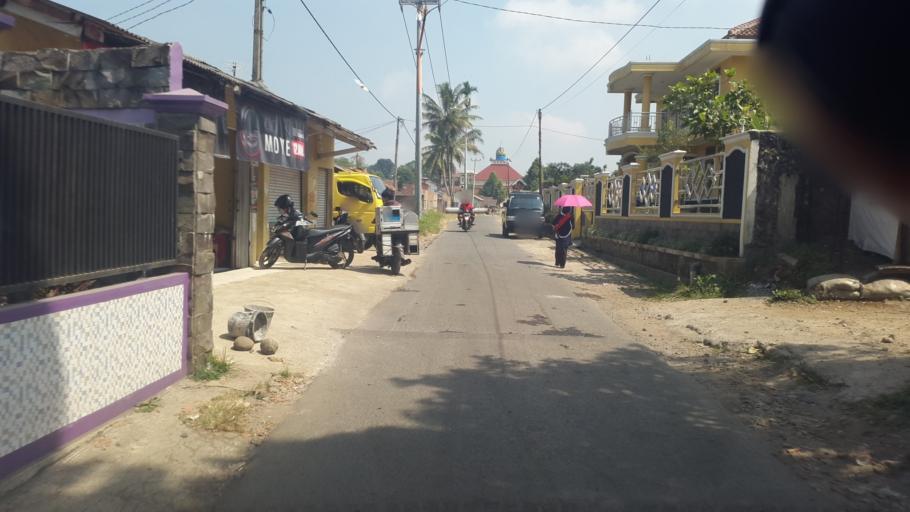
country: ID
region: West Java
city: Sukabumi
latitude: -6.8746
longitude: 106.9145
